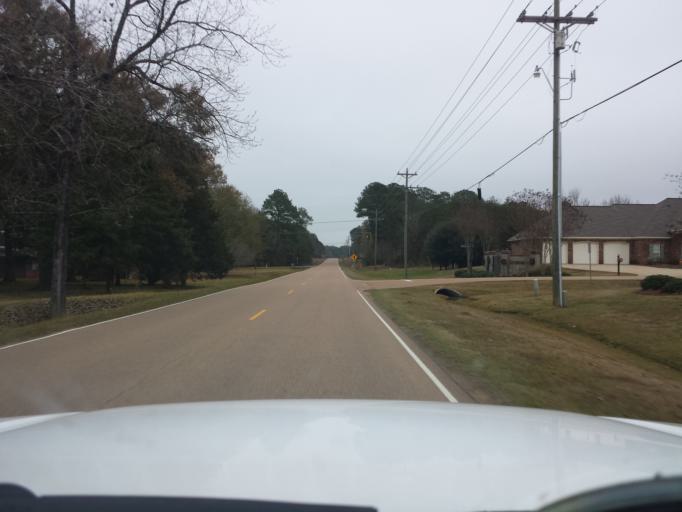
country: US
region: Mississippi
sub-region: Rankin County
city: Brandon
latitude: 32.4212
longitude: -89.9714
